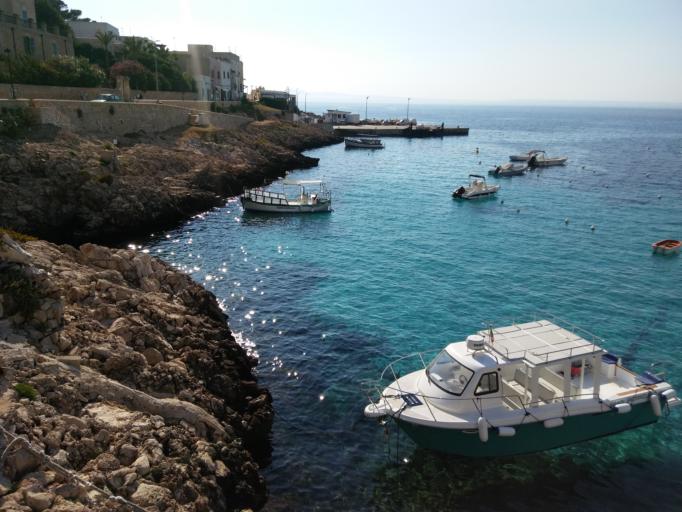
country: IT
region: Sicily
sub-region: Trapani
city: Favignana
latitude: 37.9873
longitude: 12.3403
